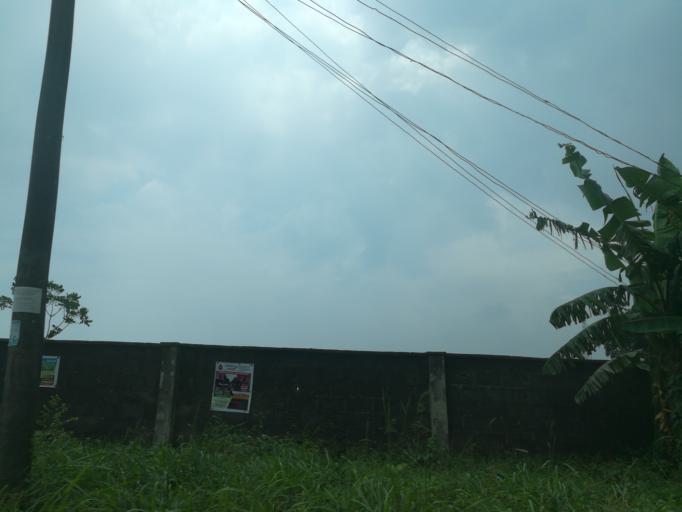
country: NG
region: Lagos
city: Ikorodu
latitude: 6.5775
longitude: 3.5909
